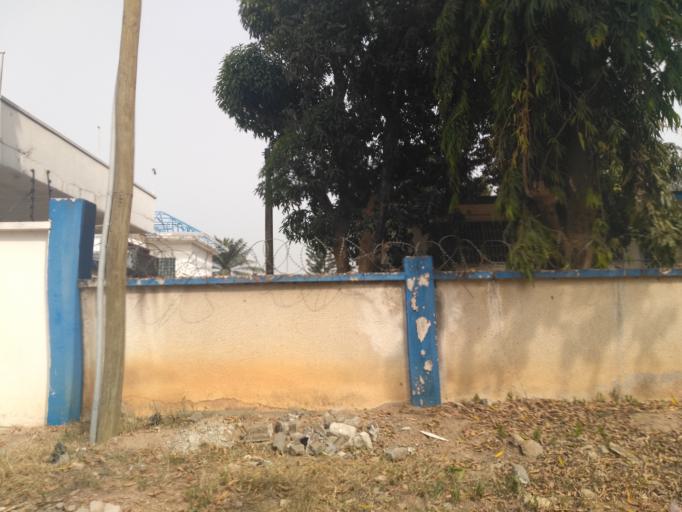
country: GH
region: Ashanti
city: Kumasi
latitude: 6.6784
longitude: -1.6045
